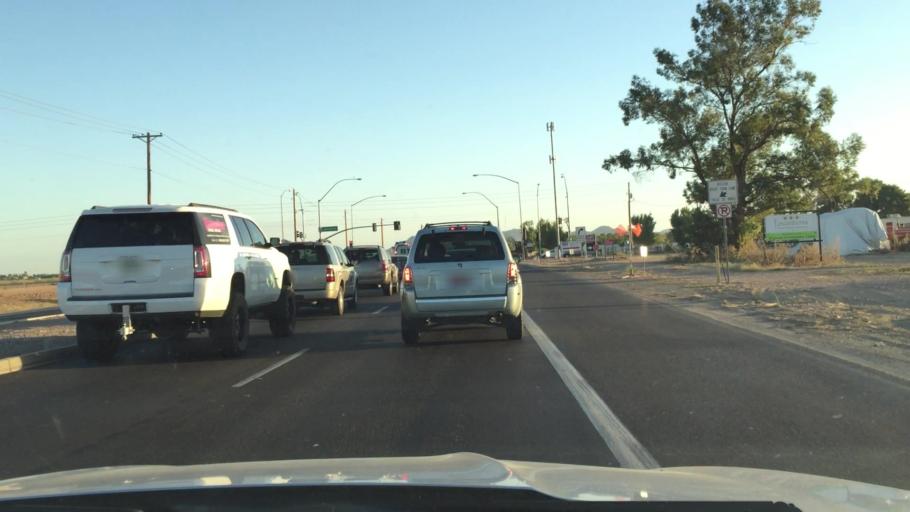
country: US
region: Arizona
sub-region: Maricopa County
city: Queen Creek
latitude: 33.2792
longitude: -111.6350
